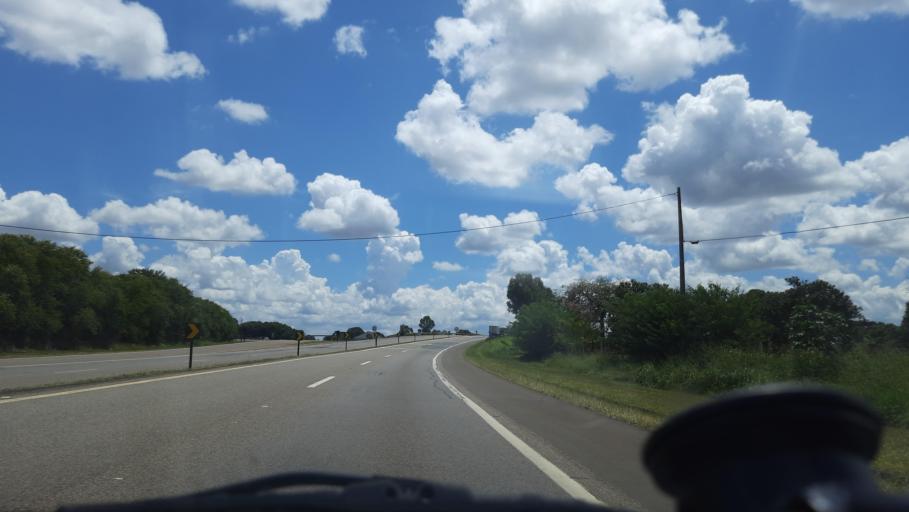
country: BR
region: Sao Paulo
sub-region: Casa Branca
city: Casa Branca
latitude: -21.7890
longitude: -47.0637
